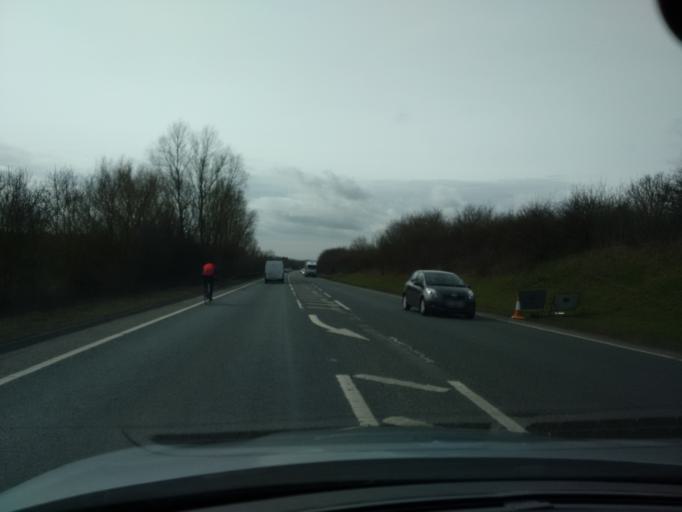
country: GB
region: England
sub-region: Worcestershire
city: Evesham
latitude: 52.0833
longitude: -1.9270
